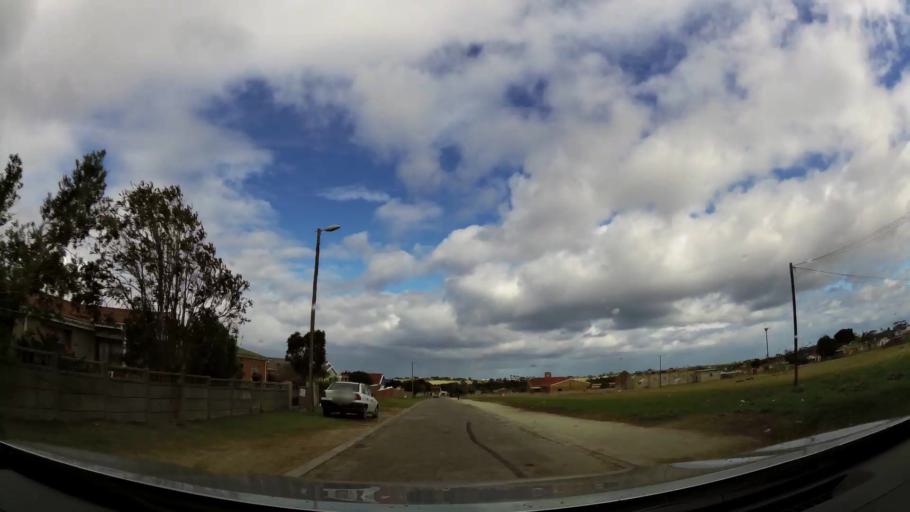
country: ZA
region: Western Cape
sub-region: Eden District Municipality
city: George
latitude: -34.0199
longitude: 22.4674
